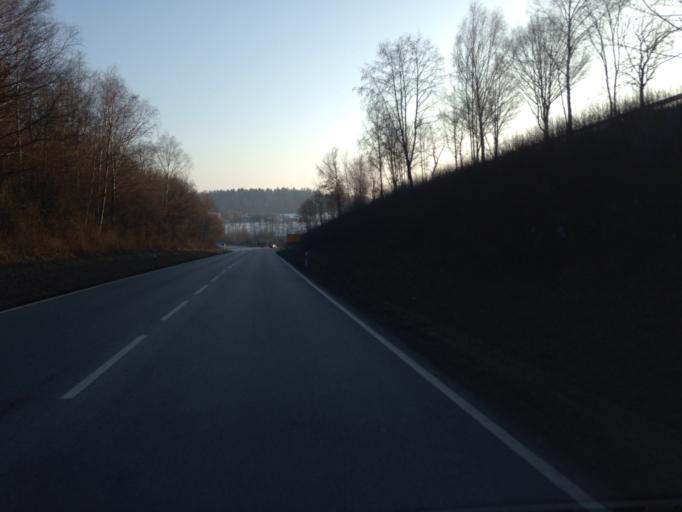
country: DE
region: Bavaria
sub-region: Lower Bavaria
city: Simbach
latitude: 48.5710
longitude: 12.7279
